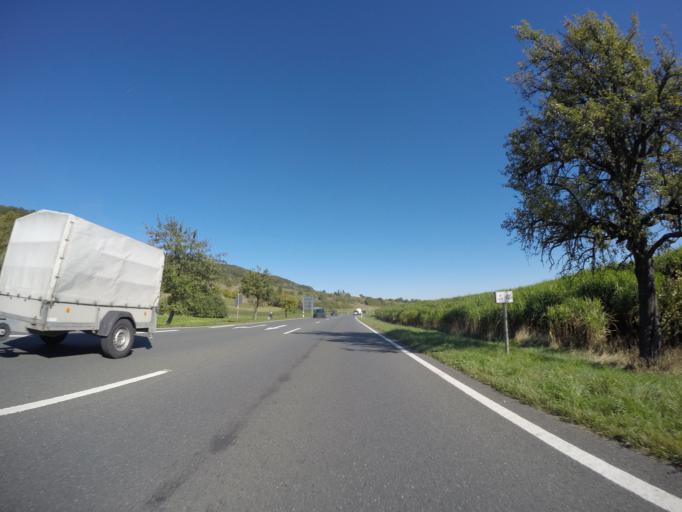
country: DE
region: Bavaria
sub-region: Upper Franconia
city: Kirchehrenbach
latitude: 49.7490
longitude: 11.1400
